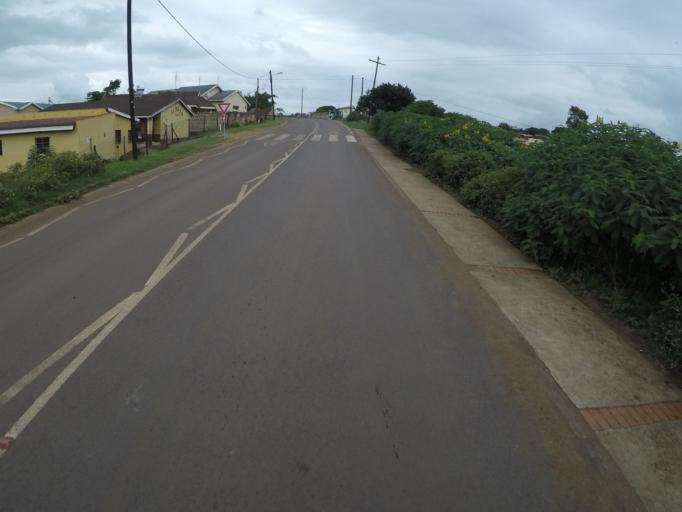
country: ZA
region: KwaZulu-Natal
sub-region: uThungulu District Municipality
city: Empangeni
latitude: -28.7730
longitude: 31.8500
